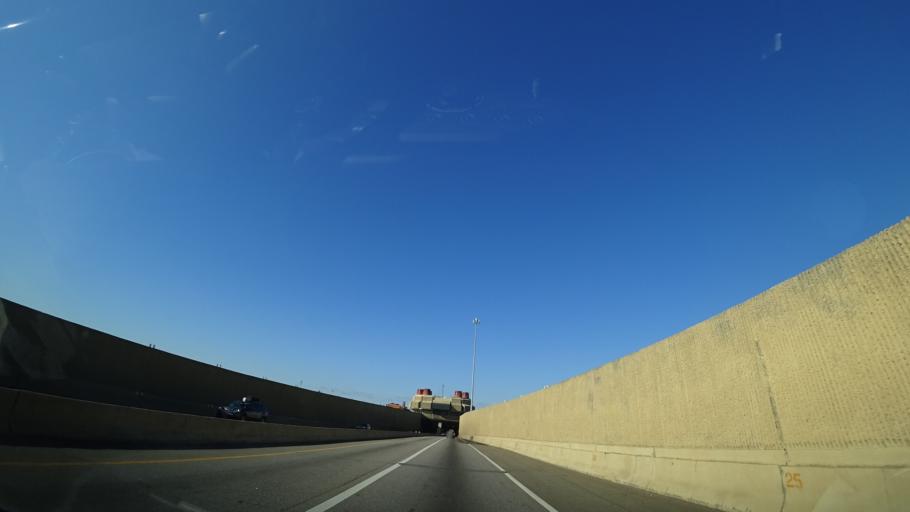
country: US
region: Virginia
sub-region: City of Newport News
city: Newport News
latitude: 36.9454
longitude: -76.4039
